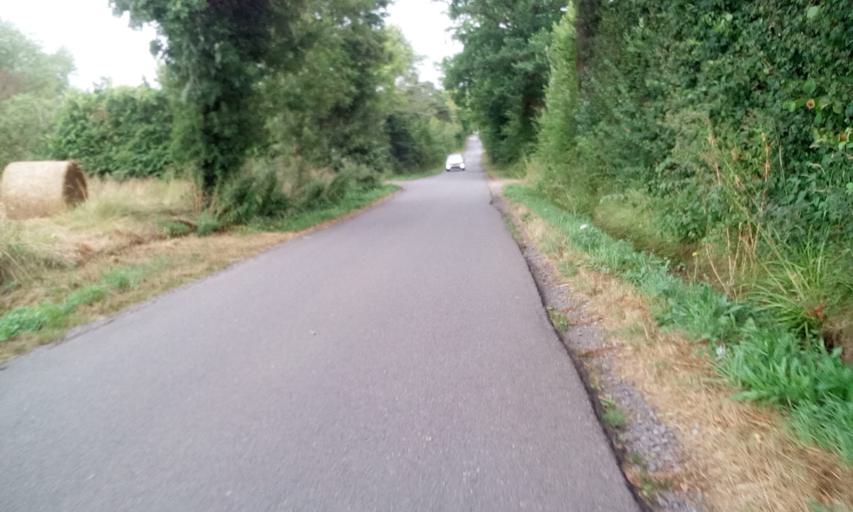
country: FR
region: Lower Normandy
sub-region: Departement du Calvados
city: Sannerville
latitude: 49.1979
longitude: -0.2228
